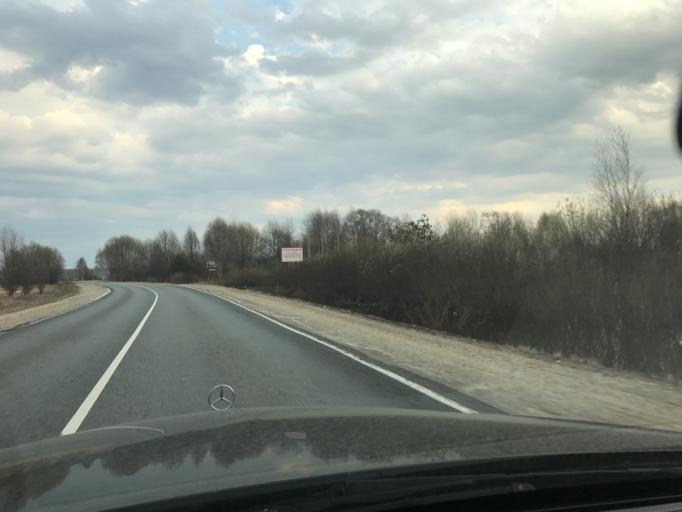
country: RU
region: Vladimir
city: Murom
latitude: 55.6289
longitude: 41.8830
